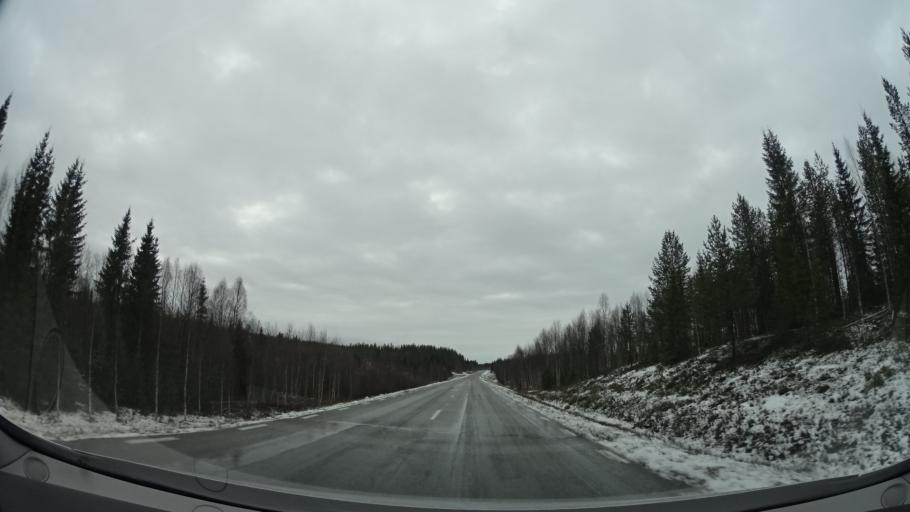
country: SE
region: Jaemtland
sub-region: Stroemsunds Kommun
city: Stroemsund
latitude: 64.0331
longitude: 15.5351
